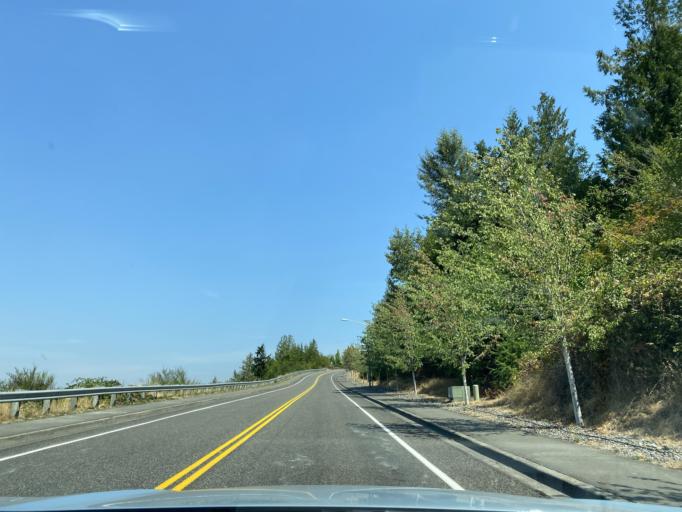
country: US
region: Washington
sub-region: Pierce County
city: Bonney Lake
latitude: 47.1584
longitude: -122.1970
